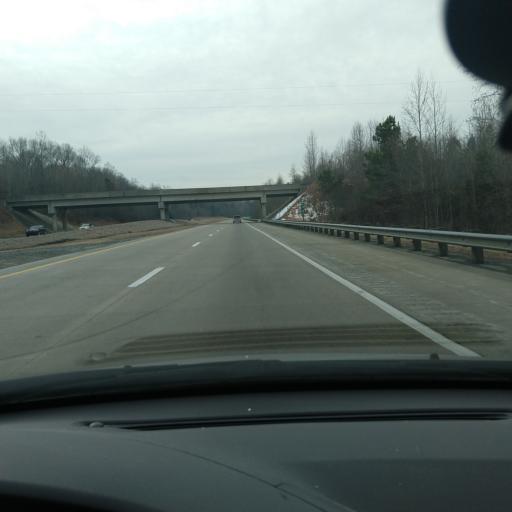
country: US
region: North Carolina
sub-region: Davidson County
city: Welcome
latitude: 35.8888
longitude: -80.2316
